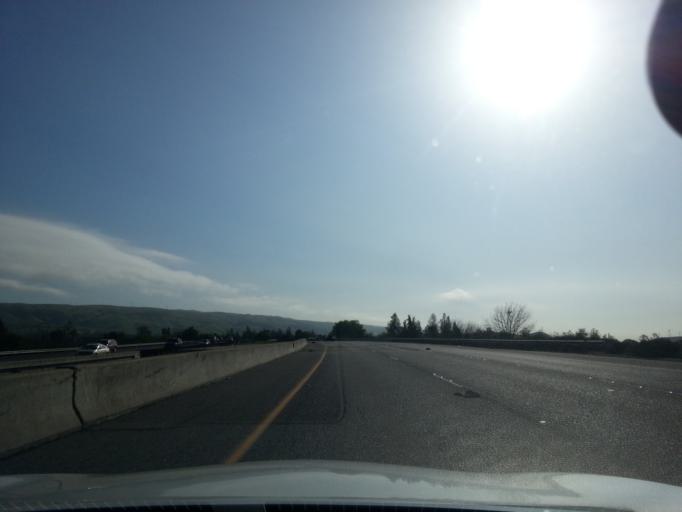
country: US
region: California
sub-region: Santa Clara County
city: Seven Trees
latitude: 37.2398
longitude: -121.7926
